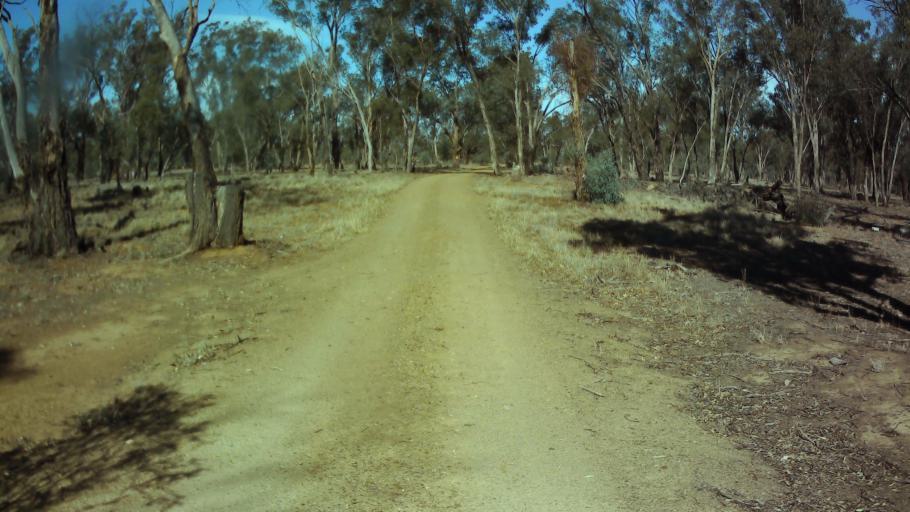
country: AU
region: New South Wales
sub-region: Weddin
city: Grenfell
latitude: -33.7337
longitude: 148.0897
